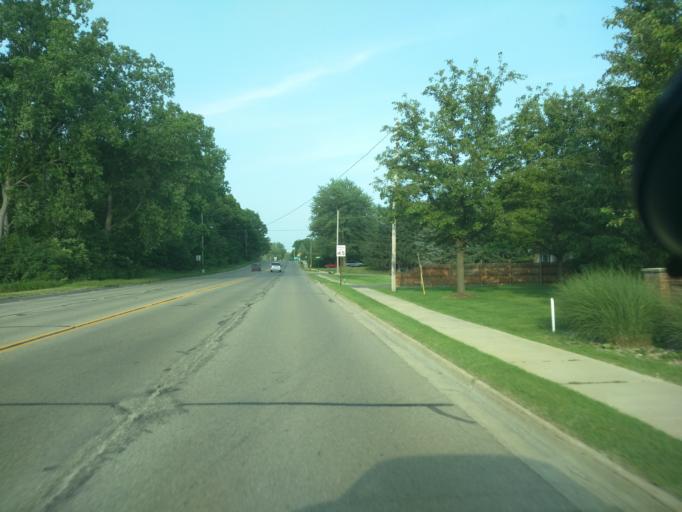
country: US
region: Michigan
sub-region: Jackson County
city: Jackson
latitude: 42.2765
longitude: -84.4386
